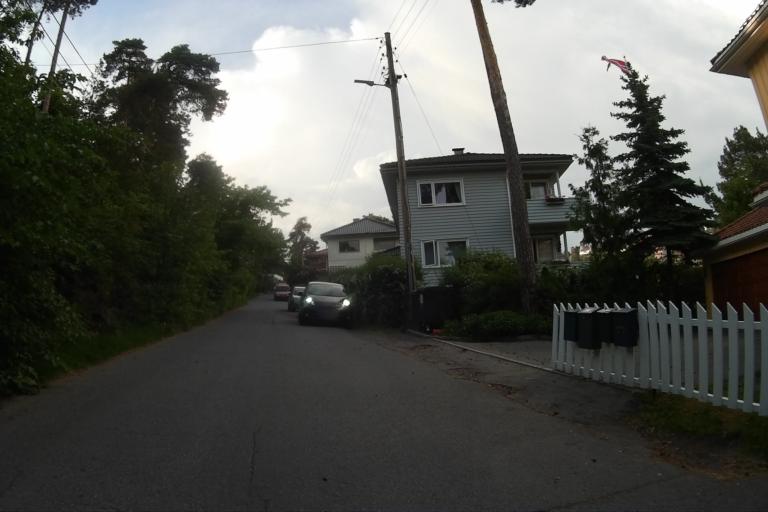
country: NO
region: Oslo
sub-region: Oslo
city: Oslo
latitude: 59.8694
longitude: 10.7754
